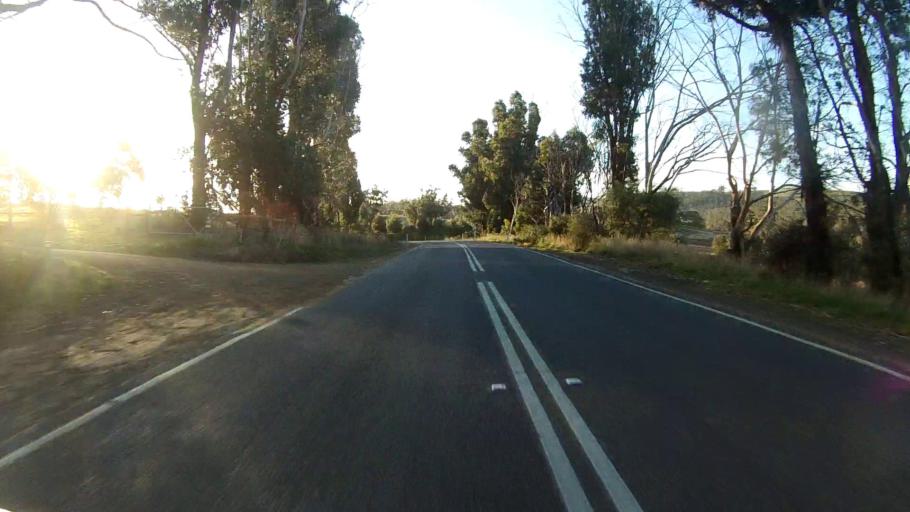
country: AU
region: Tasmania
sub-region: Sorell
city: Sorell
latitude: -42.8432
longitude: 147.8117
